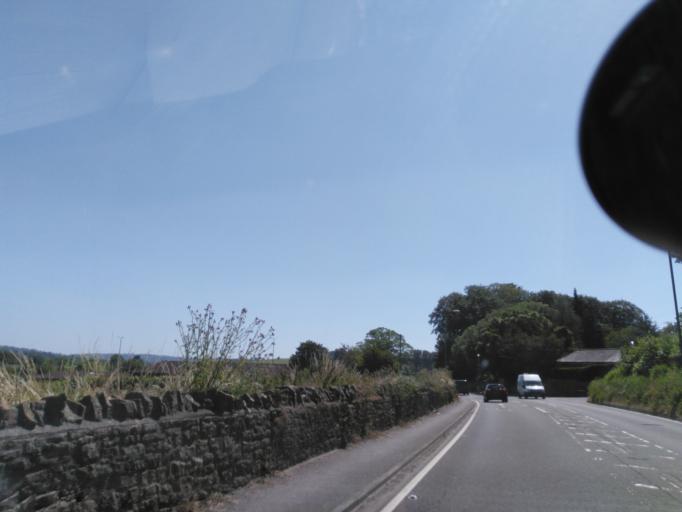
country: GB
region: England
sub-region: Bath and North East Somerset
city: Corston
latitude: 51.3915
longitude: -2.4393
